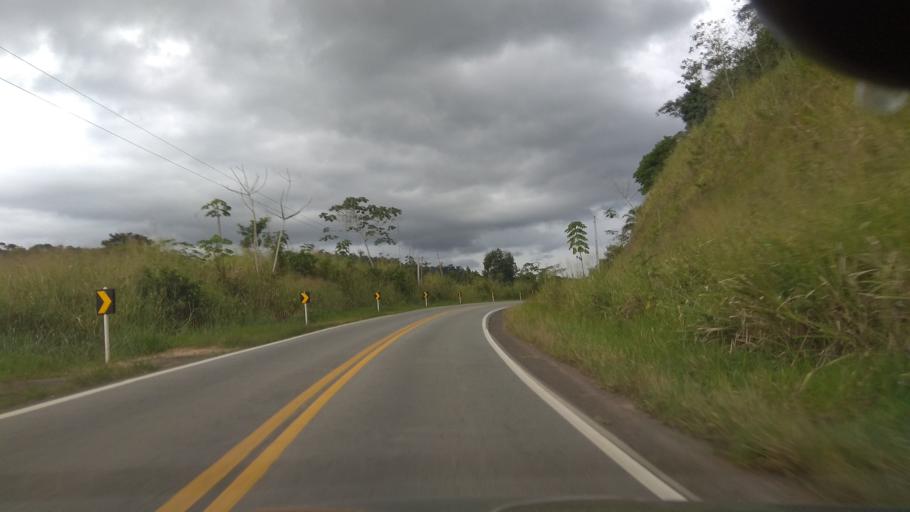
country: BR
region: Bahia
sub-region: Ubata
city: Ubata
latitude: -14.1930
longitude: -39.5599
